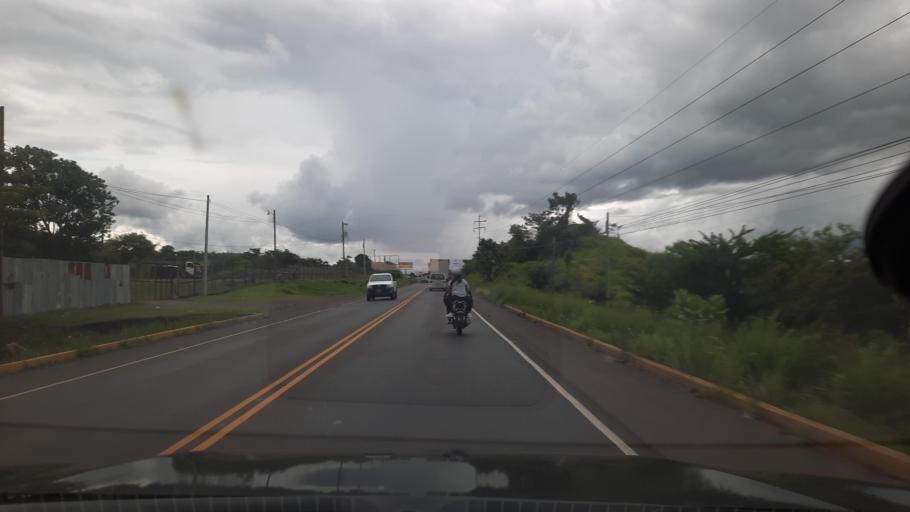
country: HN
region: Choluteca
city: Ciudad Choluteca
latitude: 13.3265
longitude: -87.2210
